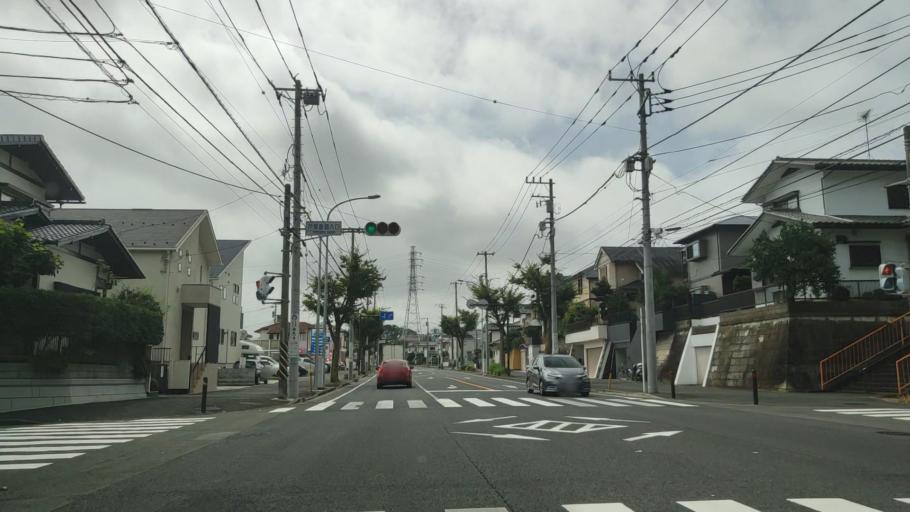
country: JP
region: Kanagawa
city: Fujisawa
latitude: 35.4128
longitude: 139.5217
